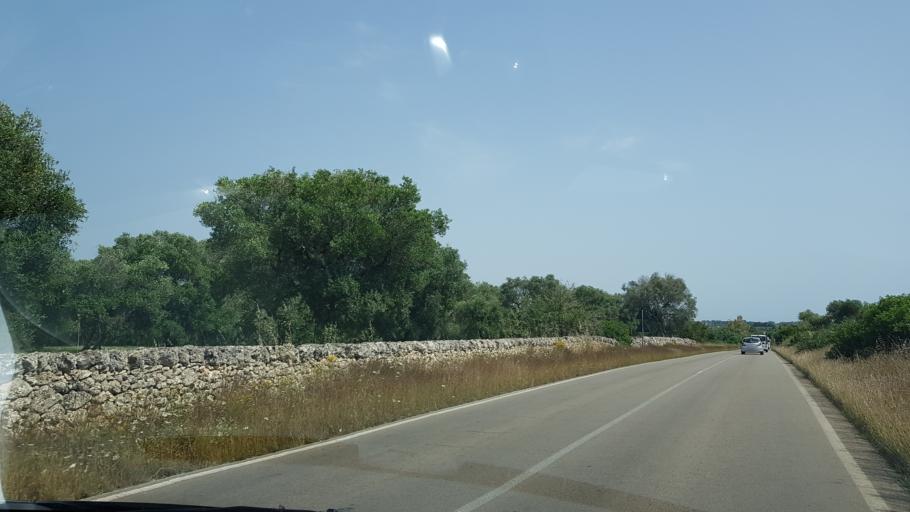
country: IT
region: Apulia
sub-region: Provincia di Lecce
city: Porto Cesareo
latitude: 40.3163
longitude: 17.8610
